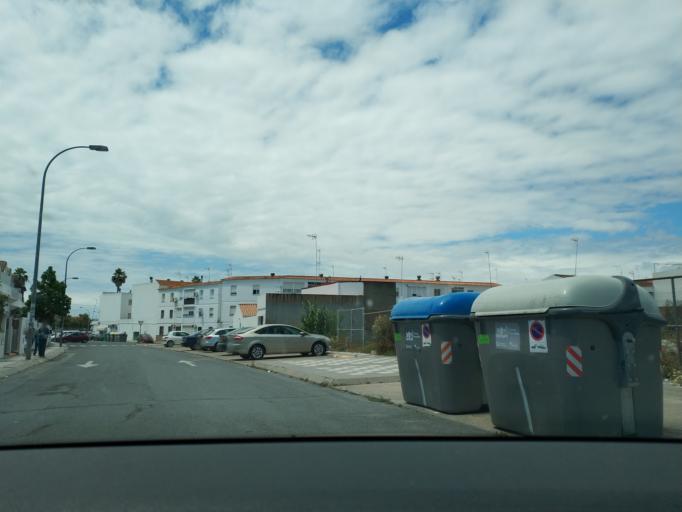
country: ES
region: Andalusia
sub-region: Provincia de Huelva
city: Cartaya
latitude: 37.2823
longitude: -7.1473
